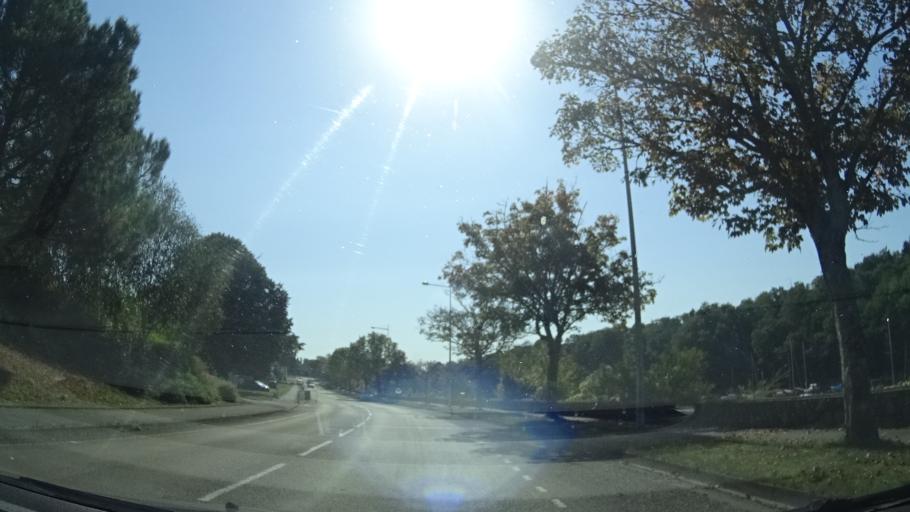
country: FR
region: Brittany
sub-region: Departement du Finistere
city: Douarnenez
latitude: 48.0851
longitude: -4.3321
